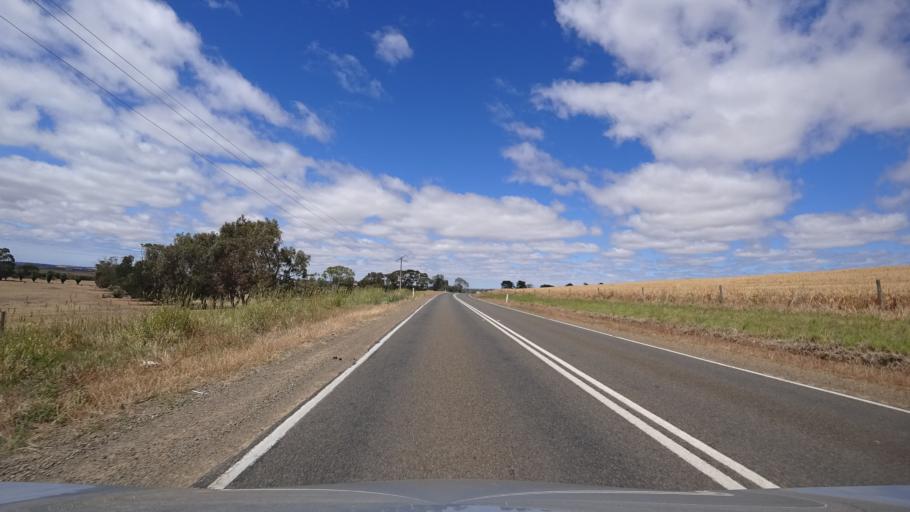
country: AU
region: South Australia
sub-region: Kangaroo Island
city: Kingscote
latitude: -35.6701
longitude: 137.5933
